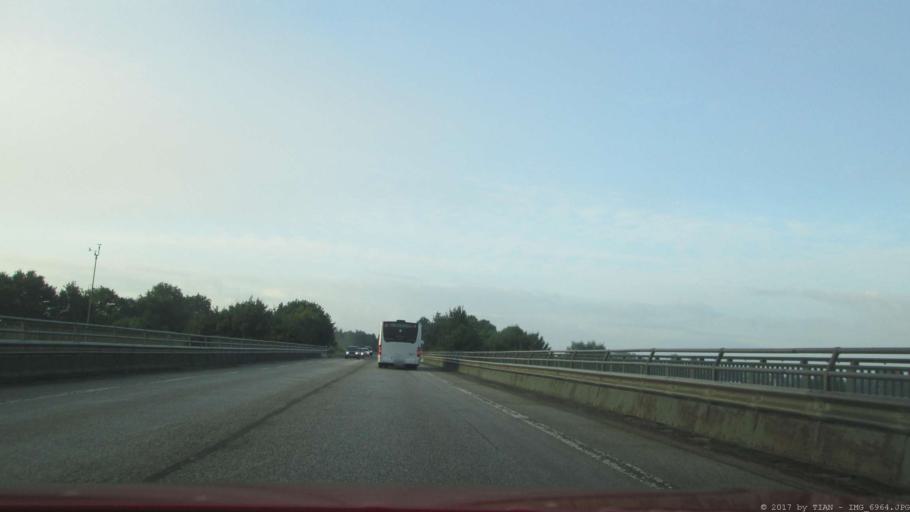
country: DE
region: Lower Saxony
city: Marschacht
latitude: 53.4247
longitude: 10.3368
